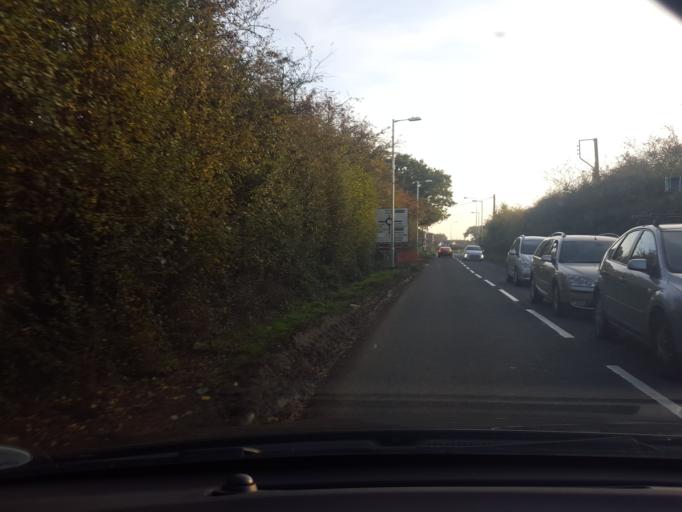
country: GB
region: England
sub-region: Essex
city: Little Clacton
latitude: 51.8203
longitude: 1.1626
